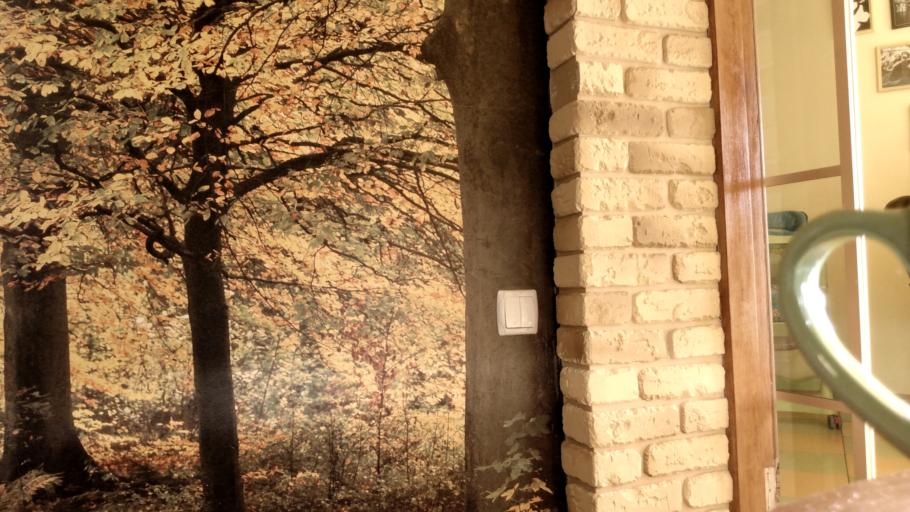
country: RU
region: Vologda
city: Imeni Zhelyabova
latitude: 58.8073
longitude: 36.8866
